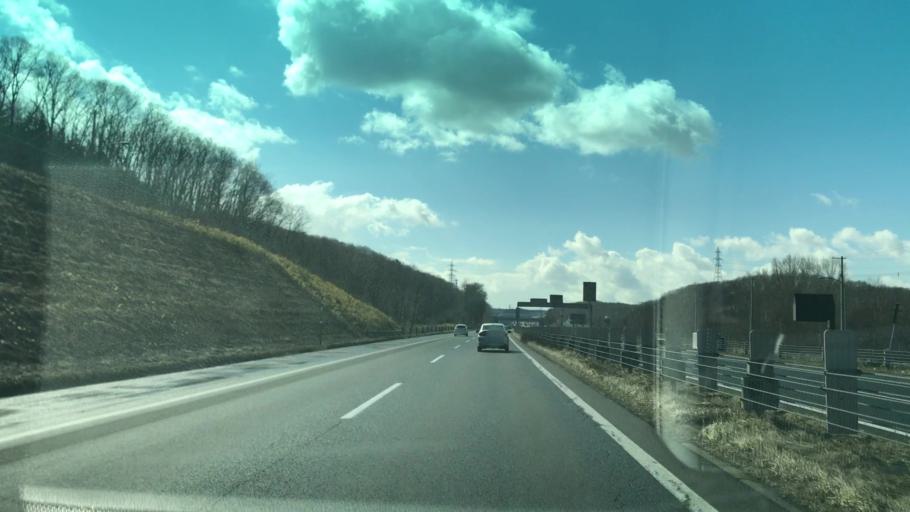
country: JP
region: Hokkaido
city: Kitahiroshima
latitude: 43.0076
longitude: 141.4666
